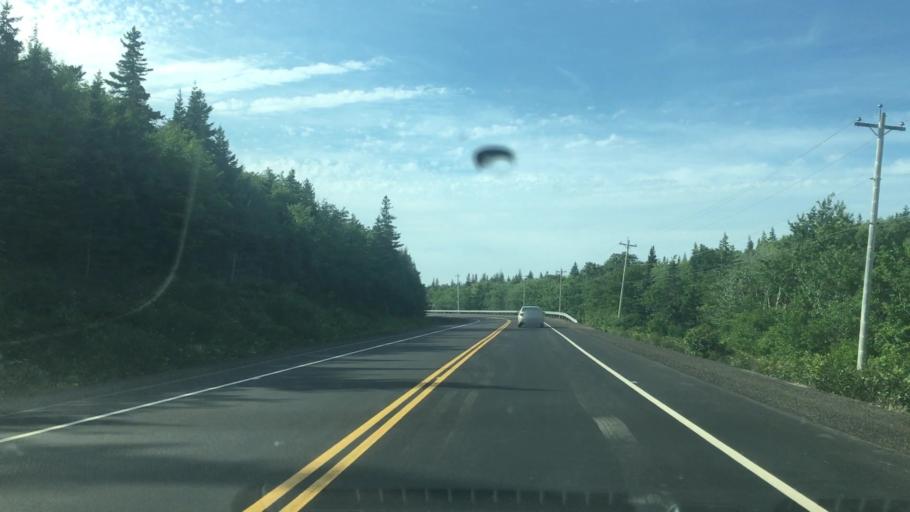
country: CA
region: Nova Scotia
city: Sydney Mines
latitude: 46.8388
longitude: -60.3866
